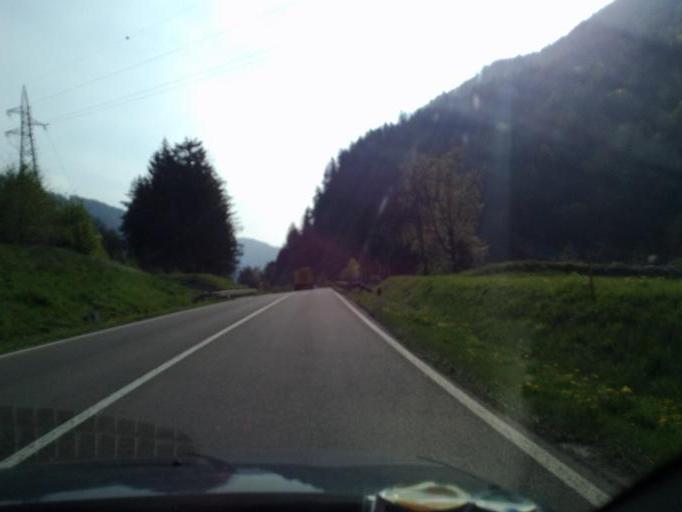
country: IT
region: Trentino-Alto Adige
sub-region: Bolzano
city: Rodengo
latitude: 46.8139
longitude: 11.6885
